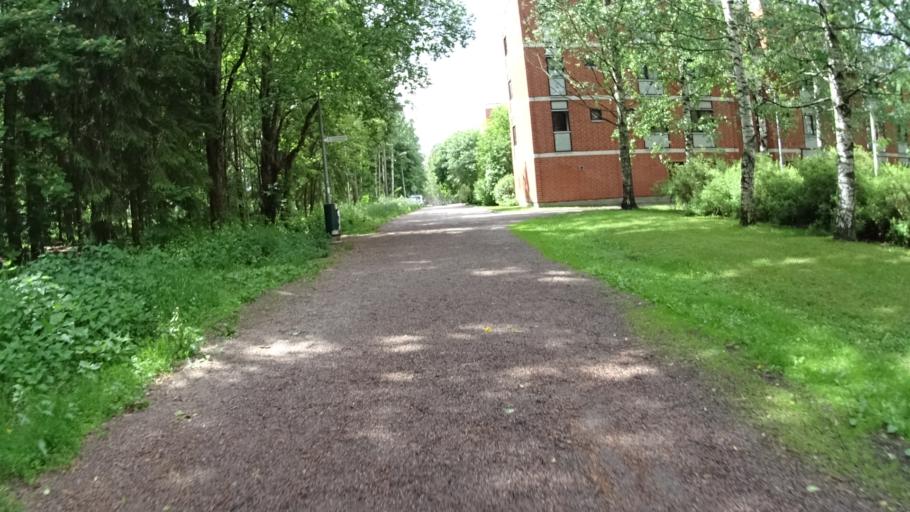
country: FI
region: Uusimaa
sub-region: Helsinki
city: Kilo
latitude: 60.2266
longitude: 24.8174
